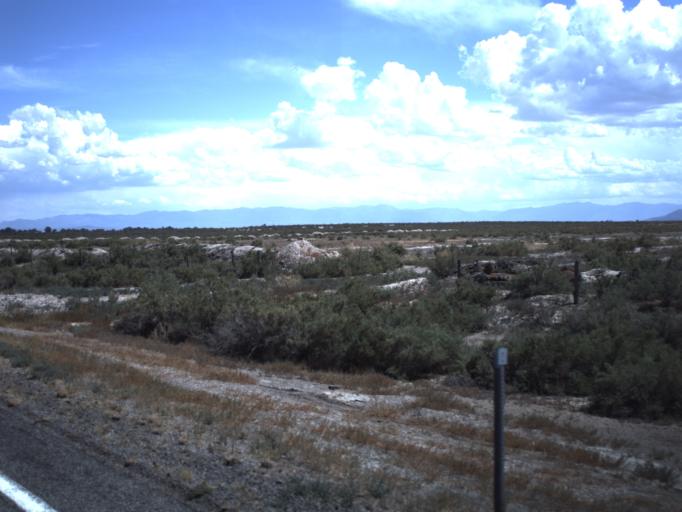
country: US
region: Utah
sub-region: Millard County
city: Delta
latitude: 39.3309
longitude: -112.7138
